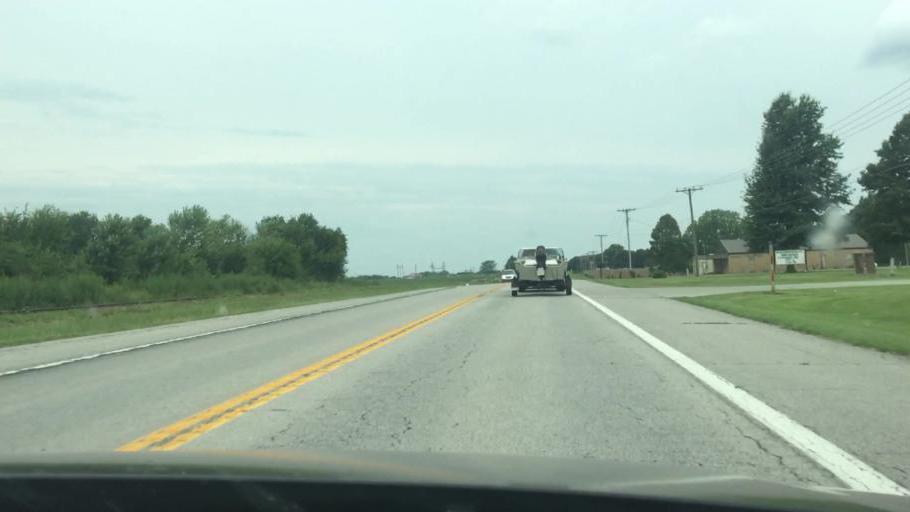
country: US
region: Missouri
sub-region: Pettis County
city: Sedalia
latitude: 38.6946
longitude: -93.1419
